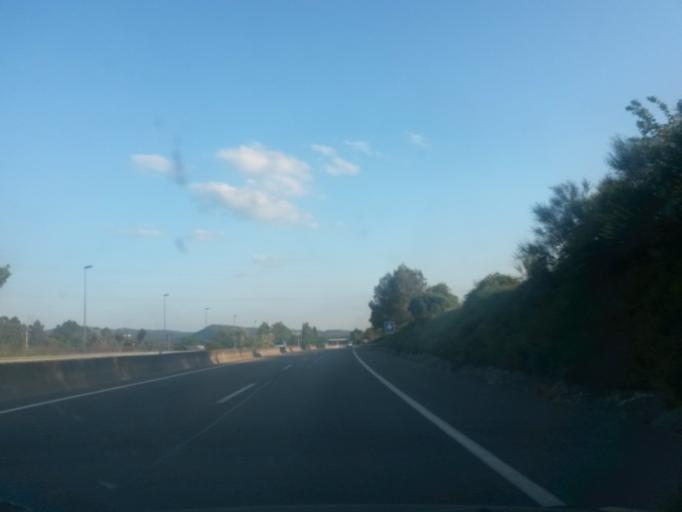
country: ES
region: Catalonia
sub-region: Provincia de Girona
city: Palol de Revardit
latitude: 42.0529
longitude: 2.8179
